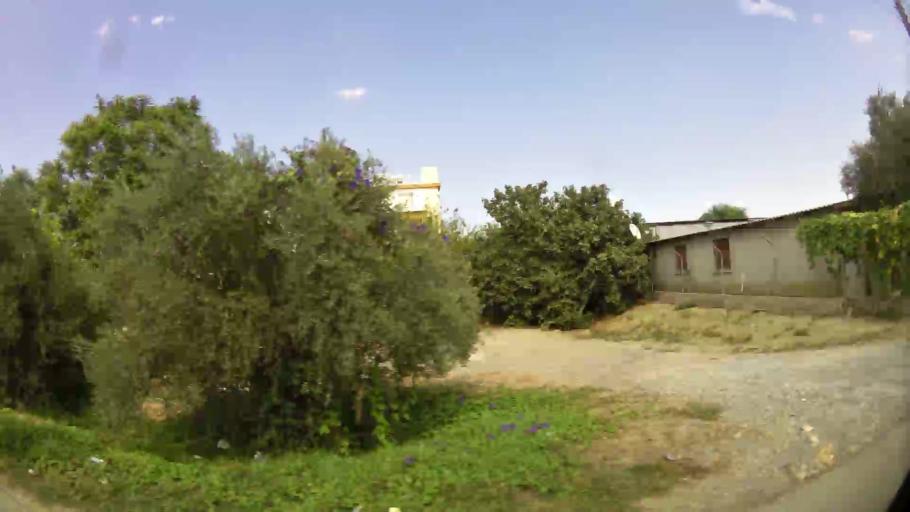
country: CY
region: Lefkosia
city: Nicosia
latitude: 35.2231
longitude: 33.3022
